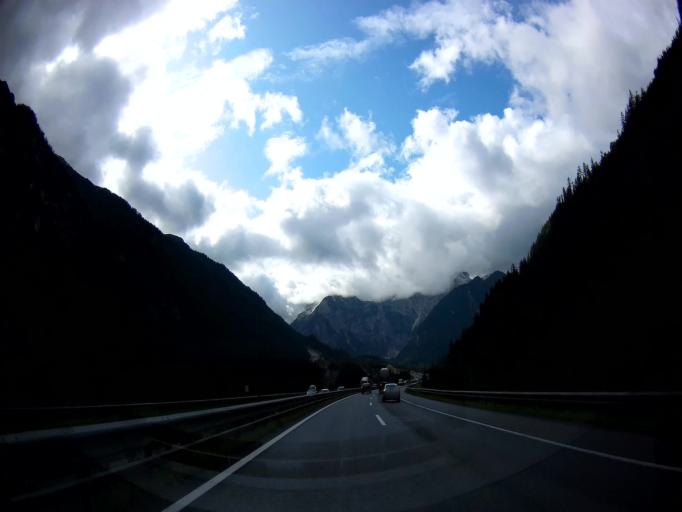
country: AT
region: Salzburg
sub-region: Politischer Bezirk Sankt Johann im Pongau
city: Flachau
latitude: 47.2779
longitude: 13.4116
